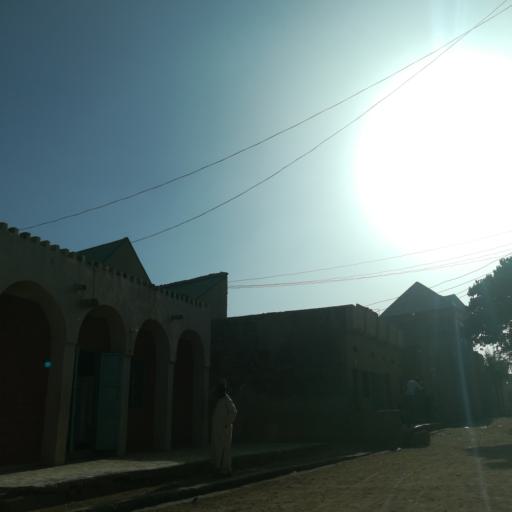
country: NG
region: Kano
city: Kano
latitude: 12.0160
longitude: 8.4943
